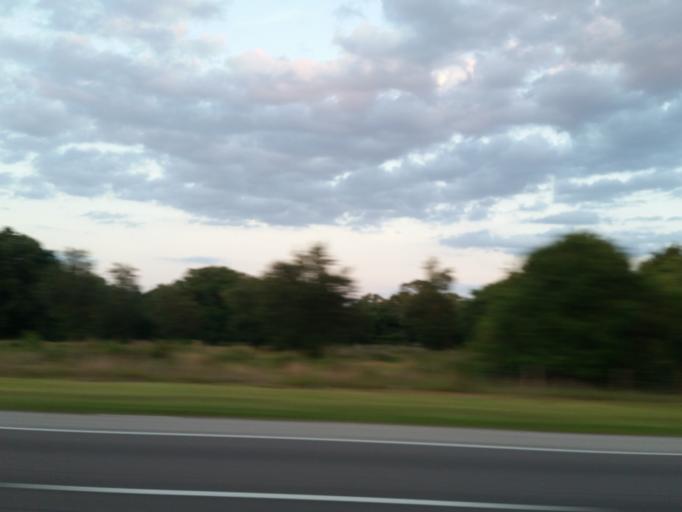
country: US
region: Florida
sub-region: Hillsborough County
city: Sun City Center
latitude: 27.7210
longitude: -82.3830
